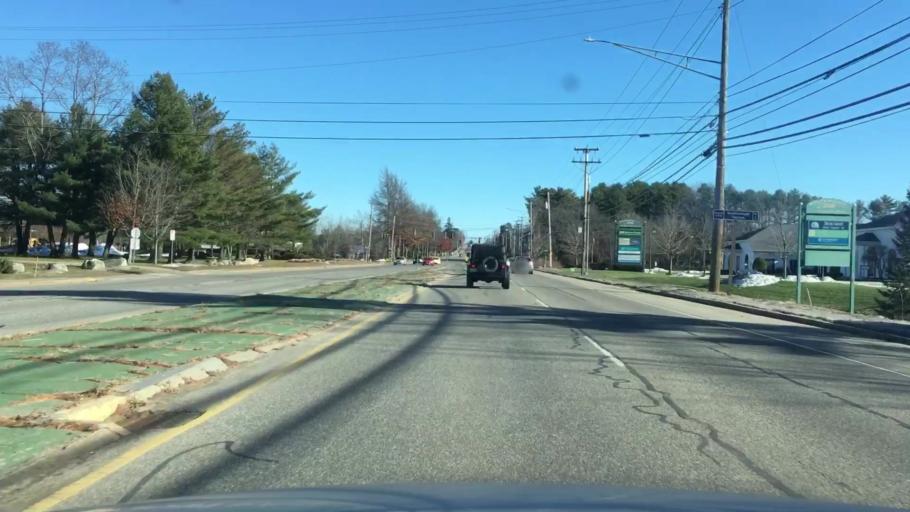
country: US
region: Maine
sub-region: Cumberland County
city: Scarborough
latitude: 43.5880
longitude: -70.3480
